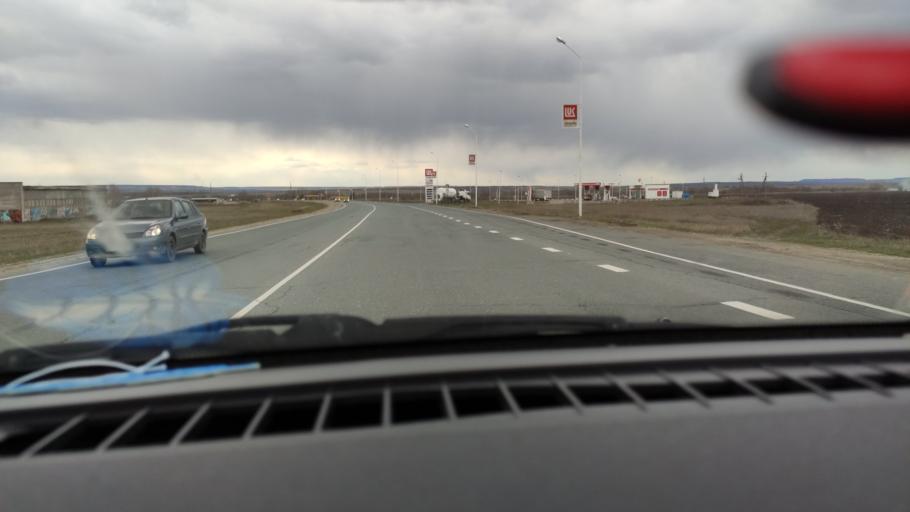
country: RU
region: Saratov
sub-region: Saratovskiy Rayon
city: Saratov
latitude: 51.7334
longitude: 46.0350
